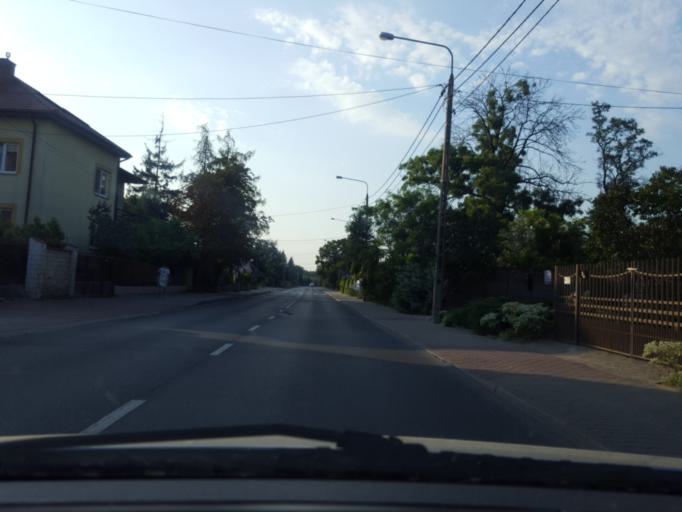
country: PL
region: Masovian Voivodeship
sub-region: Warszawa
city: Rembertow
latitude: 52.2673
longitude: 21.1538
